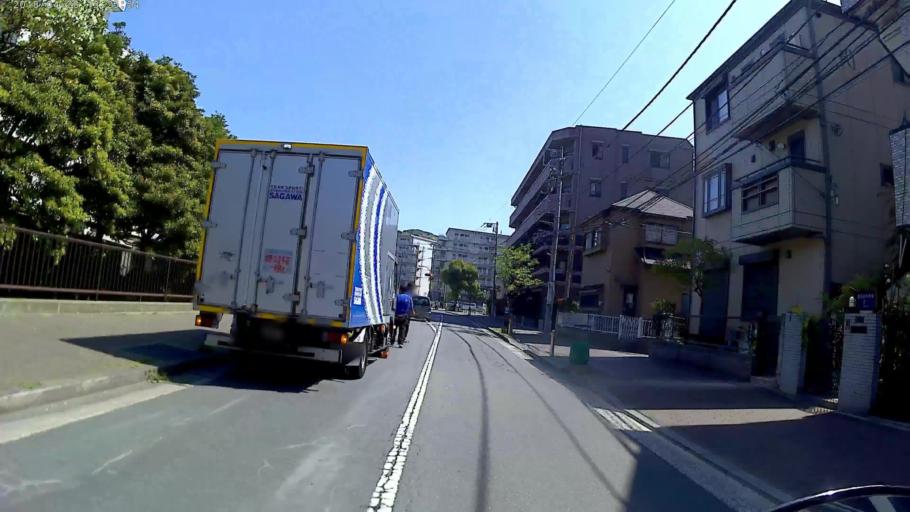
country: JP
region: Kanagawa
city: Yokosuka
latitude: 35.2291
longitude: 139.6979
